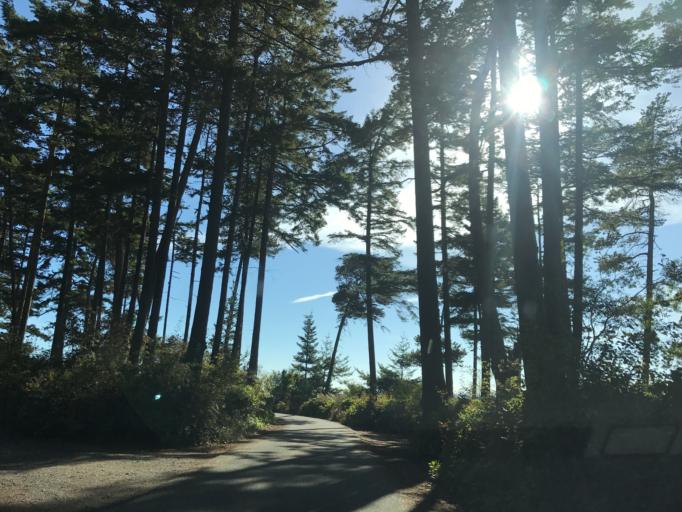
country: US
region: Washington
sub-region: Skagit County
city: Anacortes
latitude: 48.4984
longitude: -122.7007
